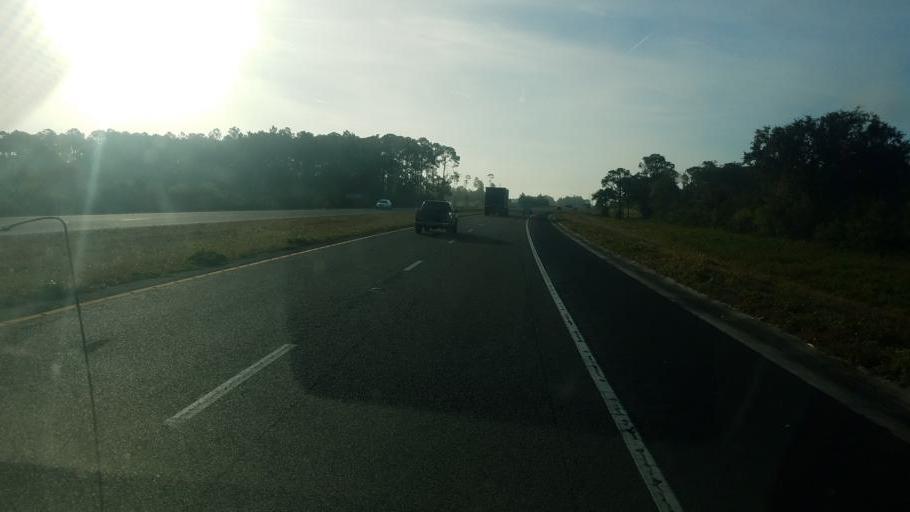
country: US
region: Florida
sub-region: Osceola County
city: Saint Cloud
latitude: 28.2305
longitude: -81.1854
